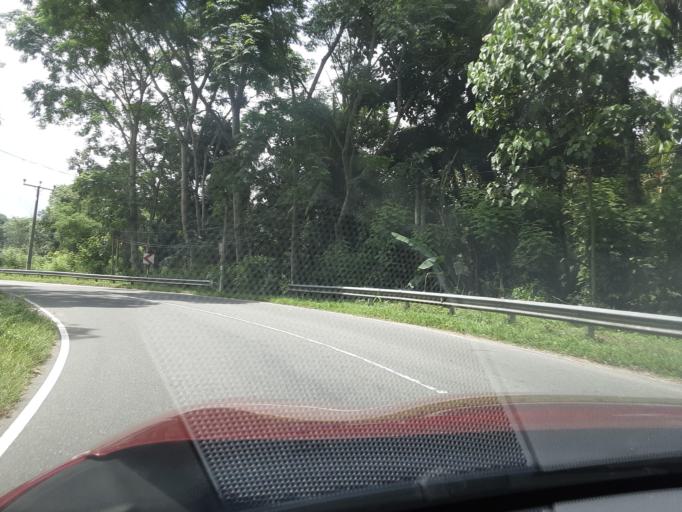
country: LK
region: Uva
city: Monaragala
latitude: 6.8980
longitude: 81.2770
